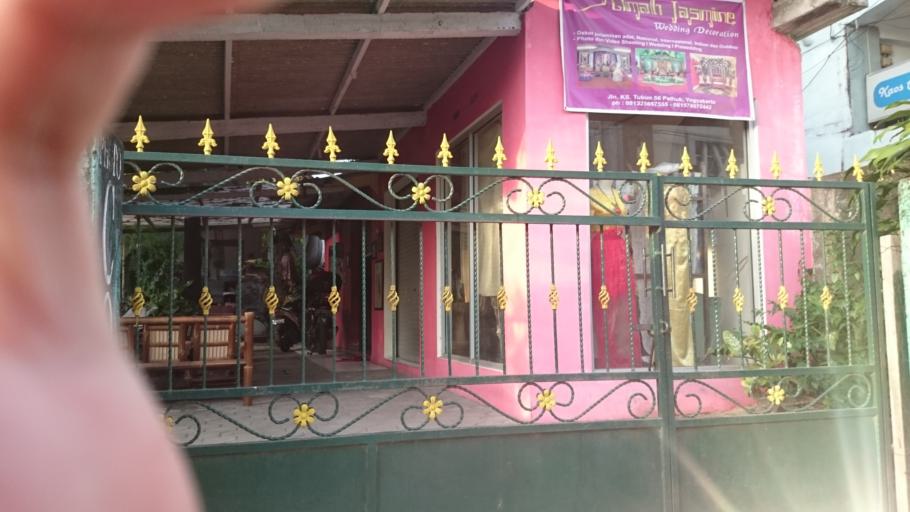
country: ID
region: Daerah Istimewa Yogyakarta
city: Yogyakarta
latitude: -7.7974
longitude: 110.3573
